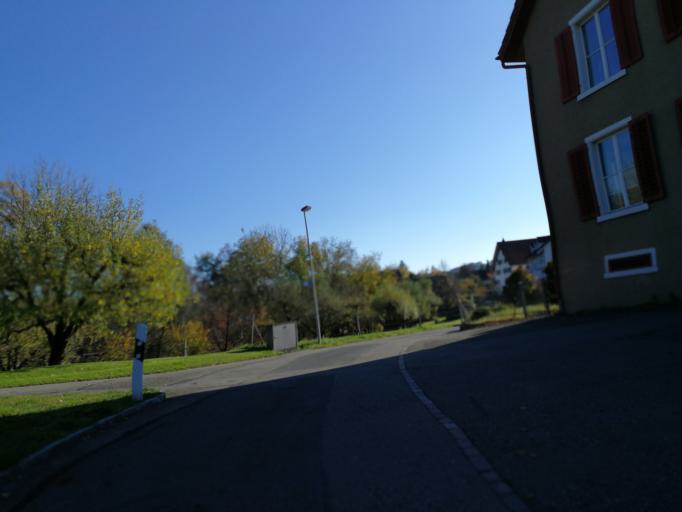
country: CH
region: Zurich
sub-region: Bezirk Uster
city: Esslingen
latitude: 47.2881
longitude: 8.7133
